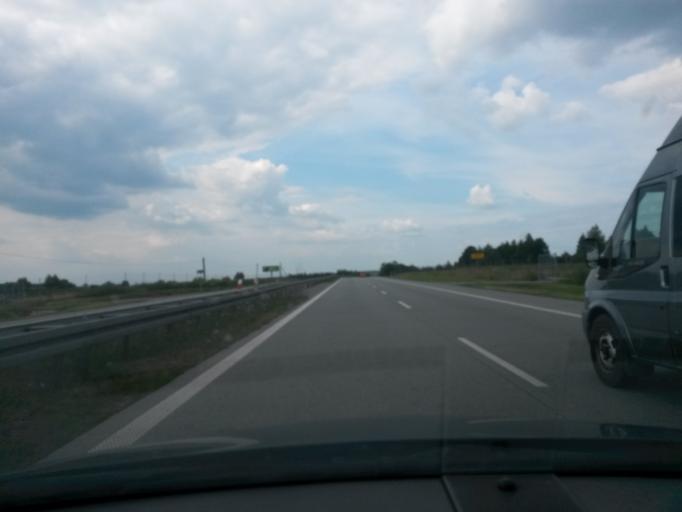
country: PL
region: Lodz Voivodeship
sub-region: Powiat skierniewicki
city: Kowiesy
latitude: 51.8719
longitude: 20.3864
